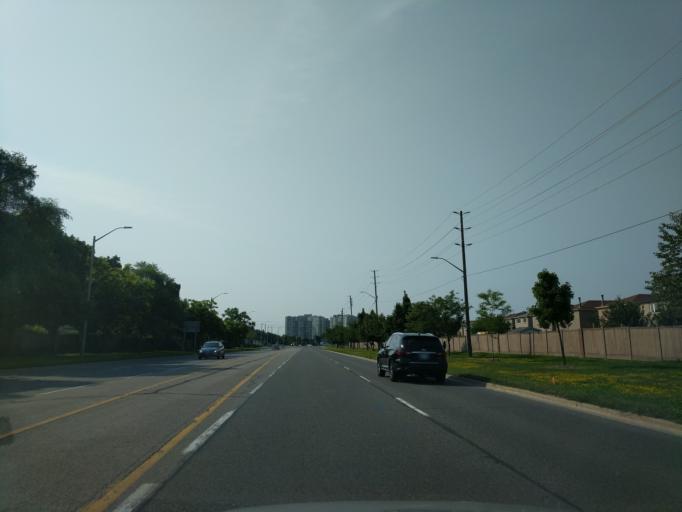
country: CA
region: Ontario
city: Markham
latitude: 43.8339
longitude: -79.2760
